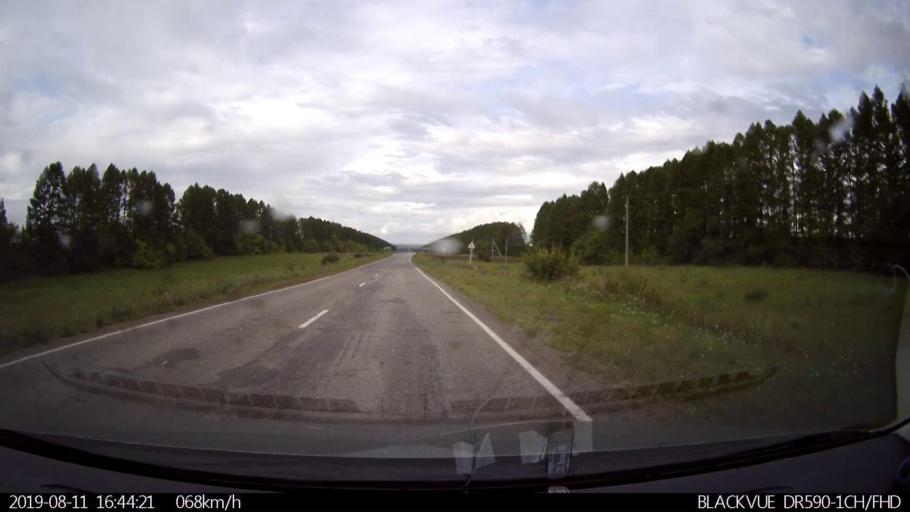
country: RU
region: Ulyanovsk
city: Mayna
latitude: 54.1780
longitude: 47.6793
